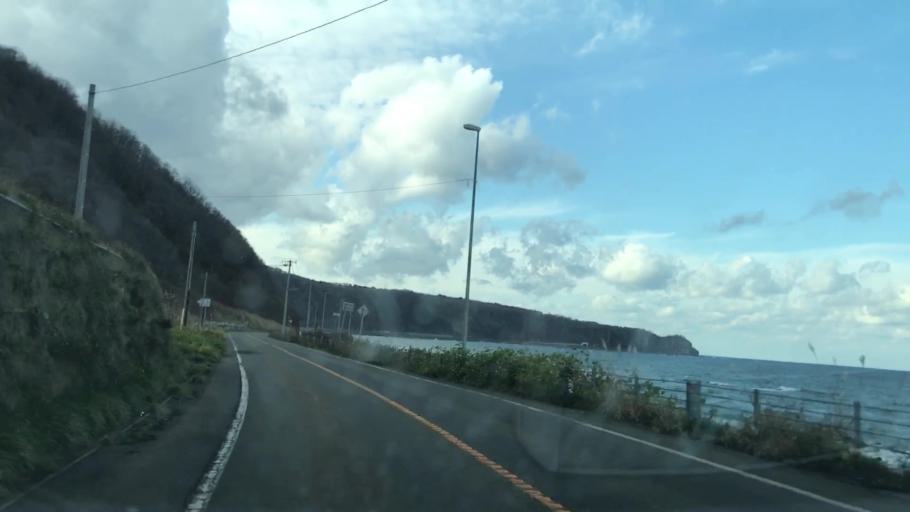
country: JP
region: Hokkaido
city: Yoichi
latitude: 43.3327
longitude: 140.4398
